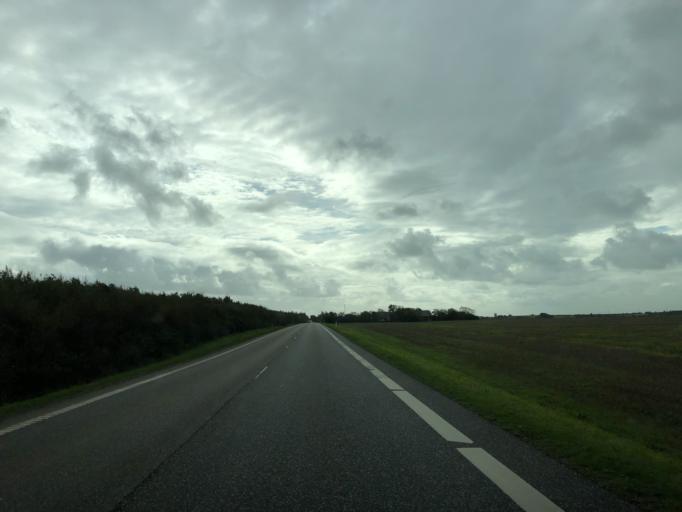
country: DK
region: North Denmark
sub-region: Thisted Kommune
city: Hurup
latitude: 56.7212
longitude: 8.4222
